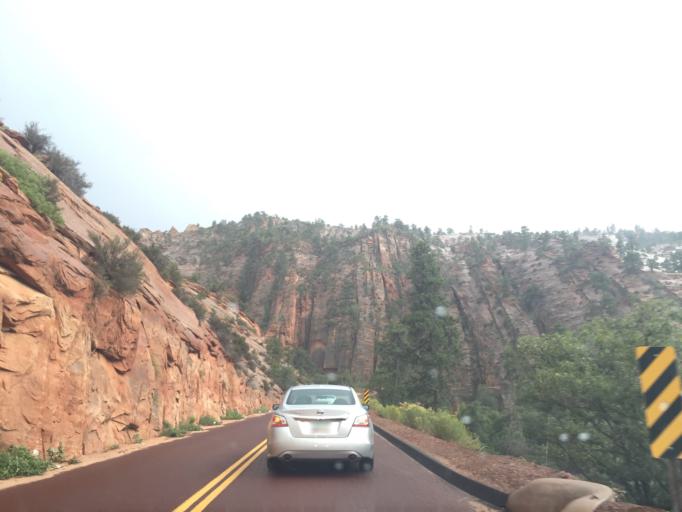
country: US
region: Utah
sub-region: Washington County
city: Hildale
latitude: 37.2177
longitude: -112.9209
